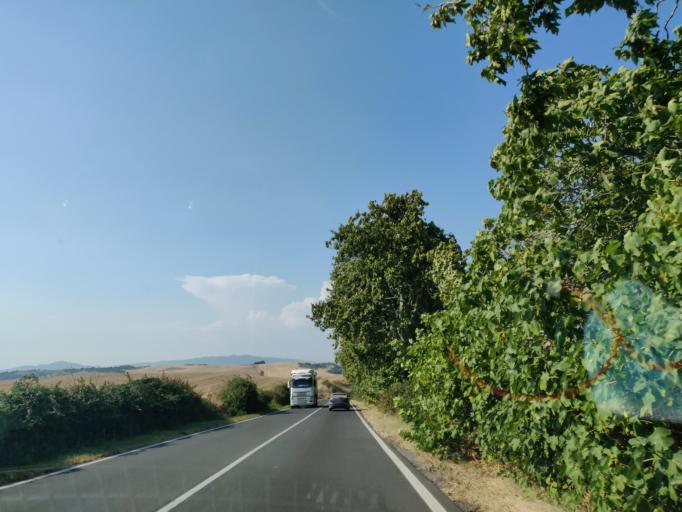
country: IT
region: Latium
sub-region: Provincia di Viterbo
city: Montalto di Castro
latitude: 42.3630
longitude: 11.6455
